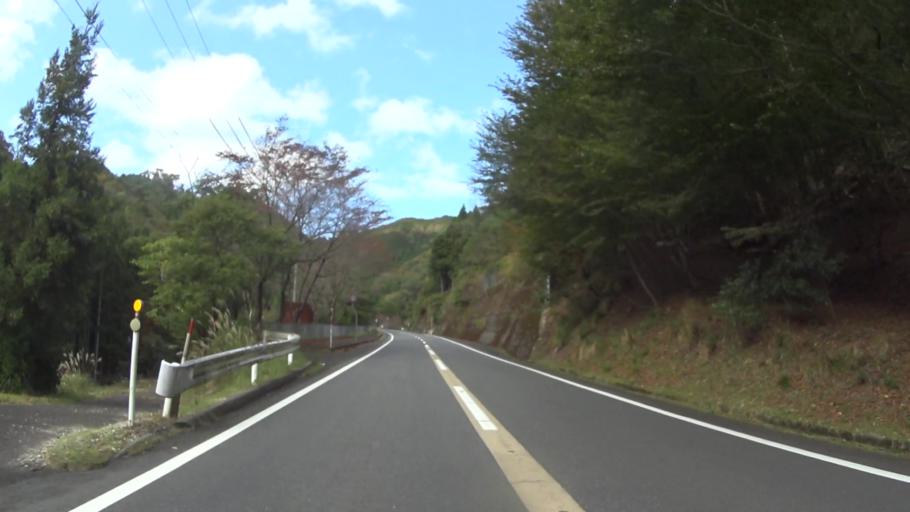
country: JP
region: Hyogo
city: Toyooka
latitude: 35.5206
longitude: 134.9889
